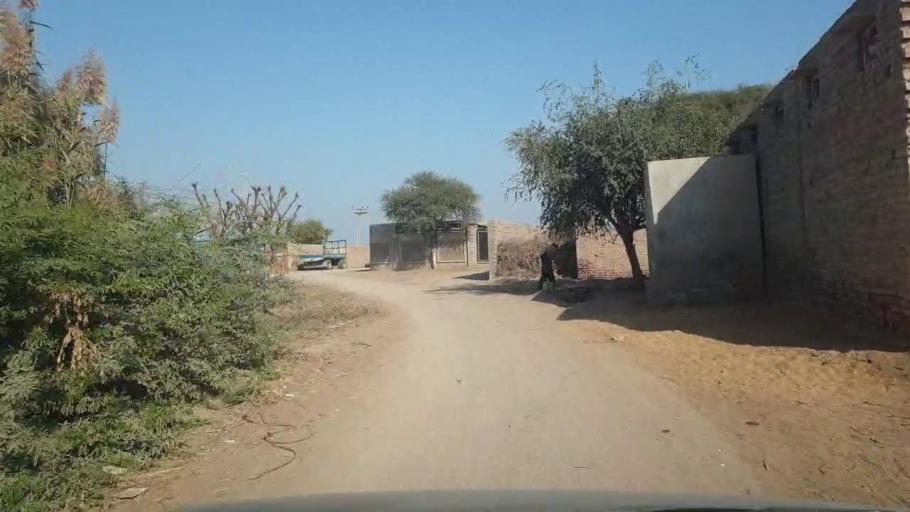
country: PK
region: Sindh
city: Chambar
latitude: 25.2879
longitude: 68.8532
